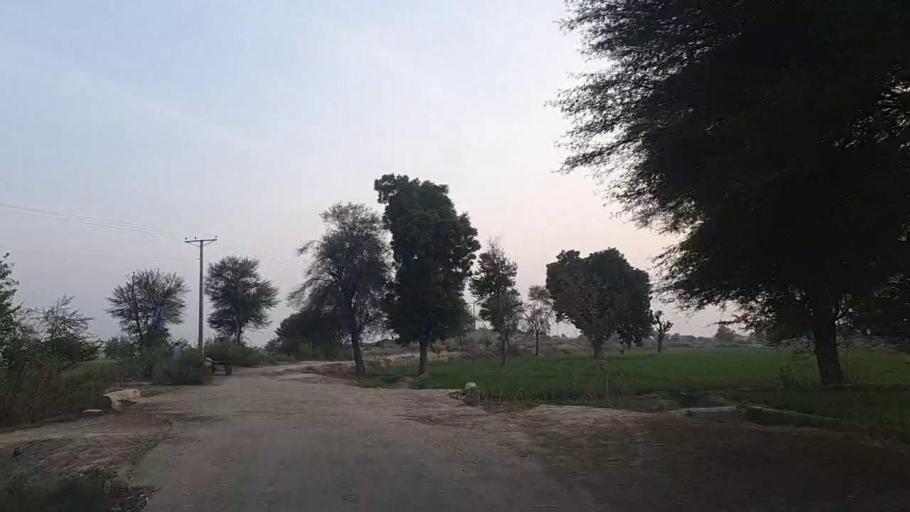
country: PK
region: Sindh
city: Jam Sahib
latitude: 26.4626
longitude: 68.5521
